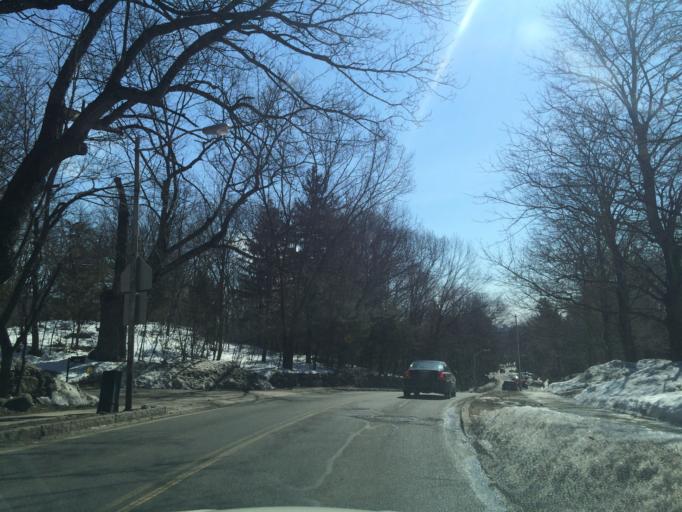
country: US
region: Massachusetts
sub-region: Middlesex County
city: Belmont
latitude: 42.4069
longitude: -71.1799
